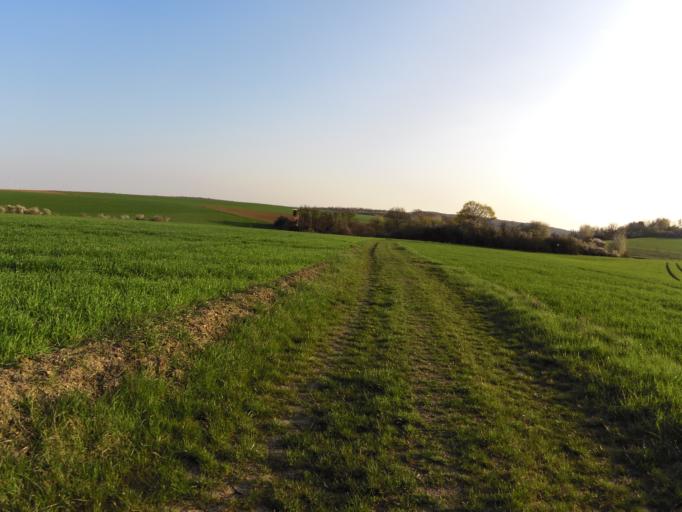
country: DE
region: Bavaria
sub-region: Regierungsbezirk Unterfranken
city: Gerbrunn
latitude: 49.7651
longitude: 10.0124
